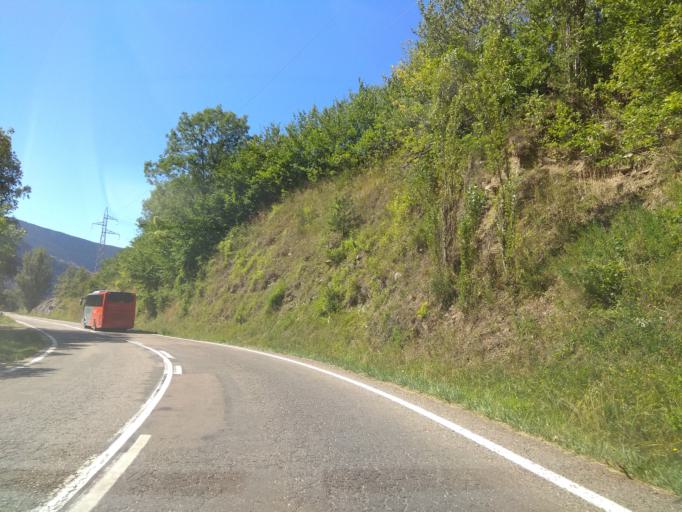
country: ES
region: Catalonia
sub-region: Provincia de Lleida
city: Vielha
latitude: 42.5312
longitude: 0.8323
